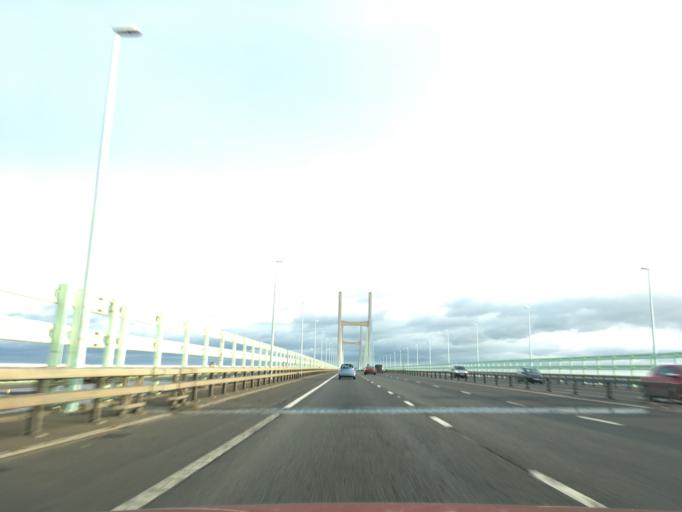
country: GB
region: Wales
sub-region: Monmouthshire
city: Caldicot
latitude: 51.5779
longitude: -2.7136
